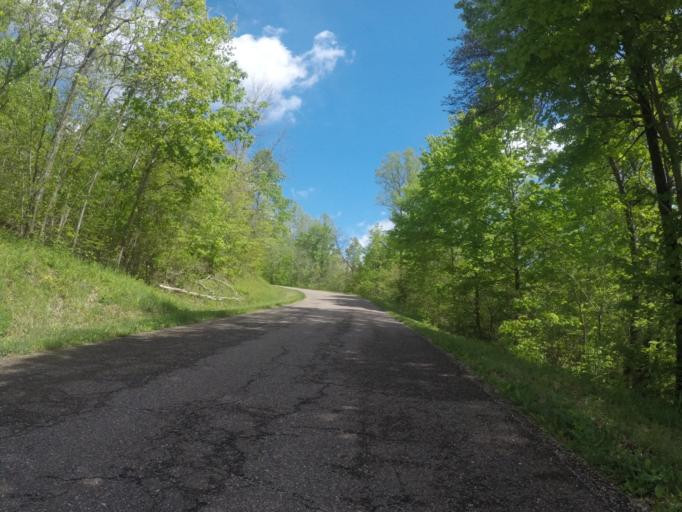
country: US
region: West Virginia
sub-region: Cabell County
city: Huntington
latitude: 38.5407
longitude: -82.4388
